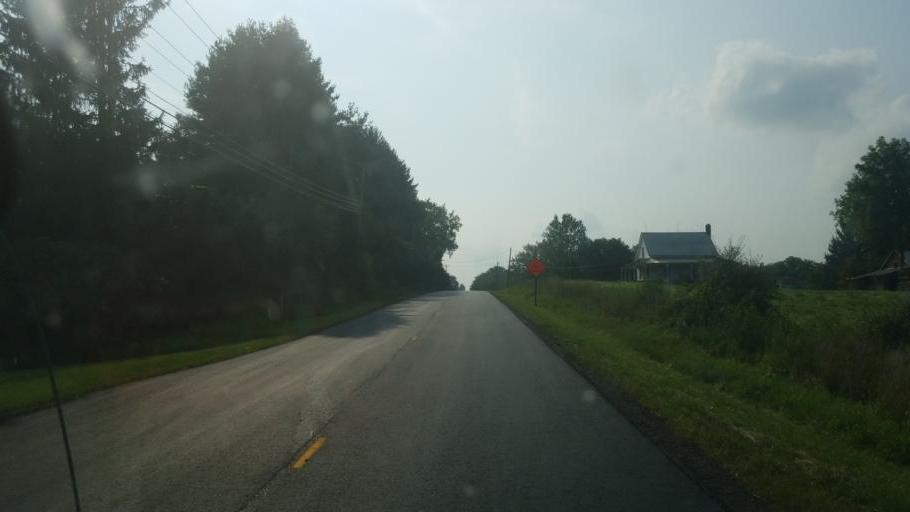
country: US
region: Ohio
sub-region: Medina County
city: Westfield Center
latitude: 41.0271
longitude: -81.9540
